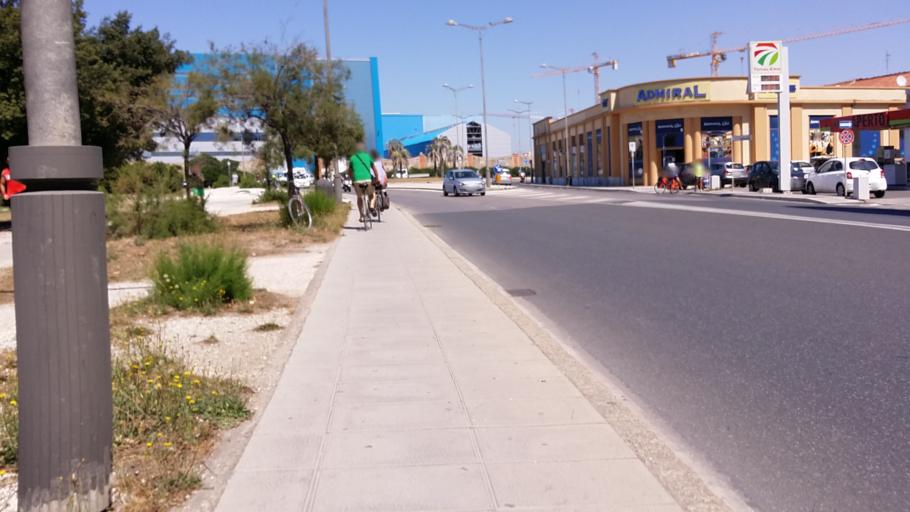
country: IT
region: Tuscany
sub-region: Provincia di Livorno
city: Livorno
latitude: 43.5401
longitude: 10.3018
